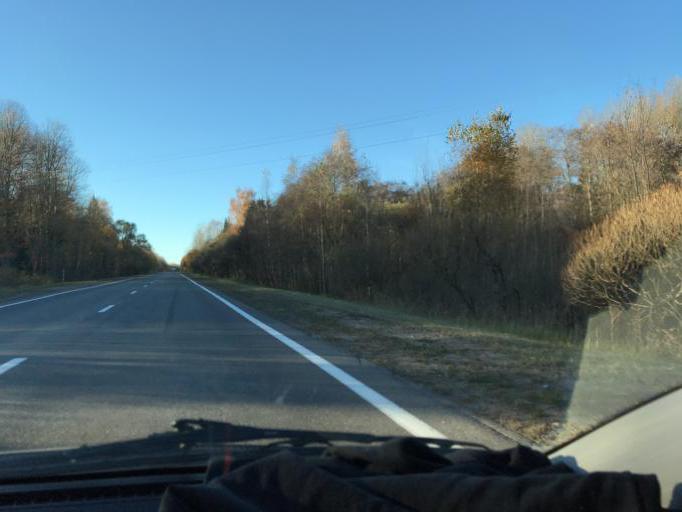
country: BY
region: Vitebsk
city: Vitebsk
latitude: 55.3542
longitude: 30.1906
